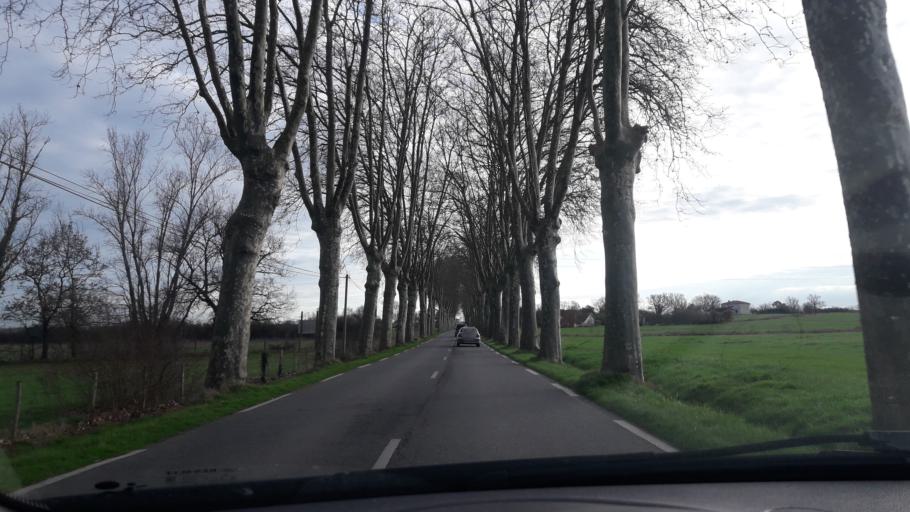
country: FR
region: Midi-Pyrenees
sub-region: Departement de la Haute-Garonne
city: Grenade
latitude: 43.7506
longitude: 1.2719
